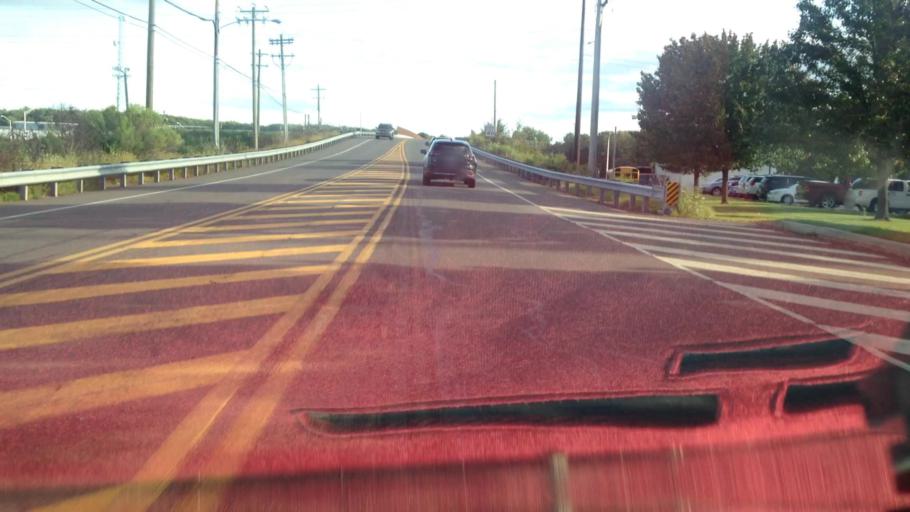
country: US
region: Pennsylvania
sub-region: Bucks County
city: Penndel
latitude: 40.1302
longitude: -74.9427
